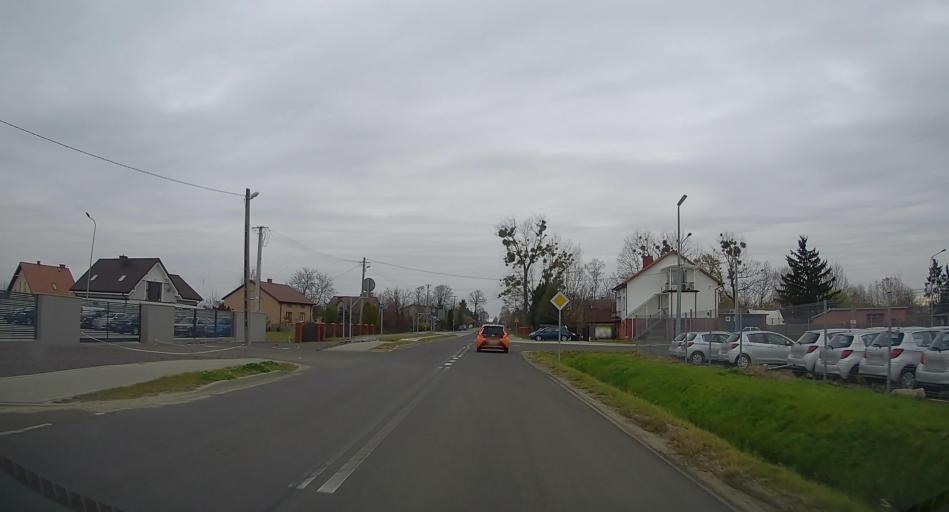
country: PL
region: Masovian Voivodeship
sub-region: Powiat zyrardowski
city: Radziejowice
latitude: 52.0054
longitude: 20.5938
